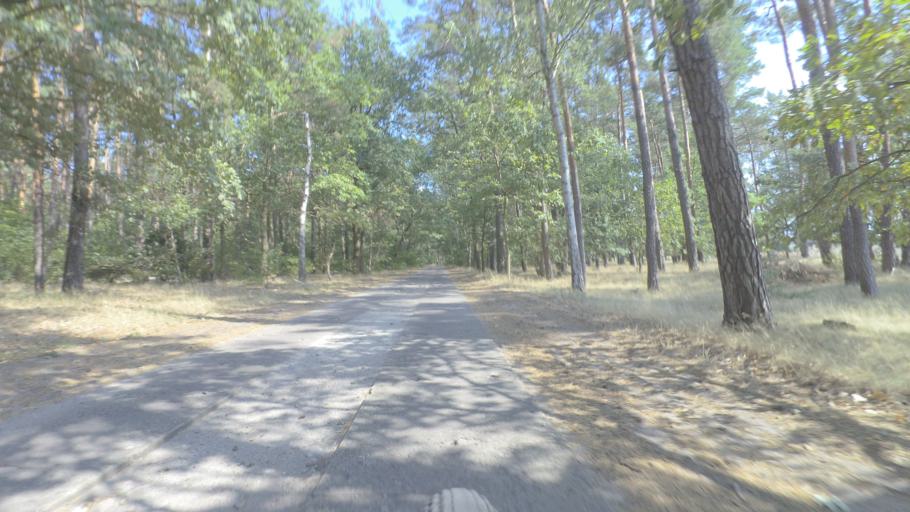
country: DE
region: Brandenburg
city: Sperenberg
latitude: 52.1916
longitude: 13.3353
